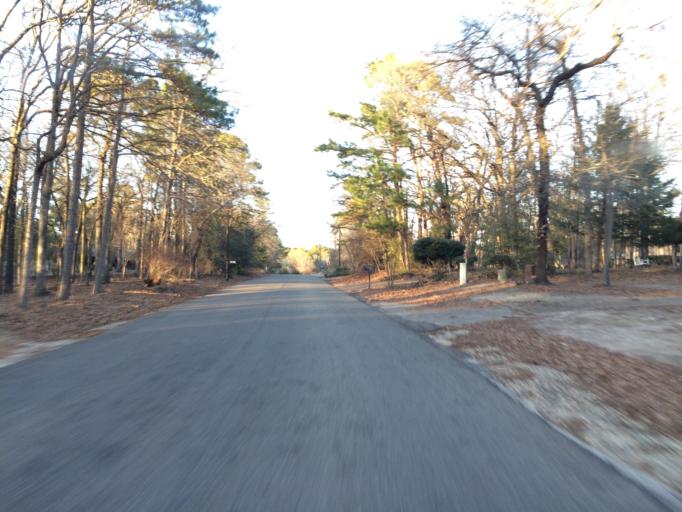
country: US
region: Texas
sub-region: Wood County
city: Hawkins
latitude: 32.7229
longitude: -95.1915
